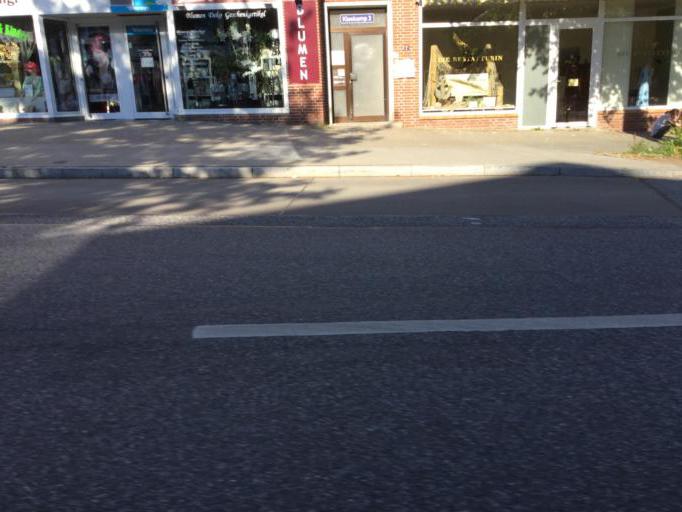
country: DE
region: Hamburg
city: Ohlsdorf
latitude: 53.6322
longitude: 10.0259
